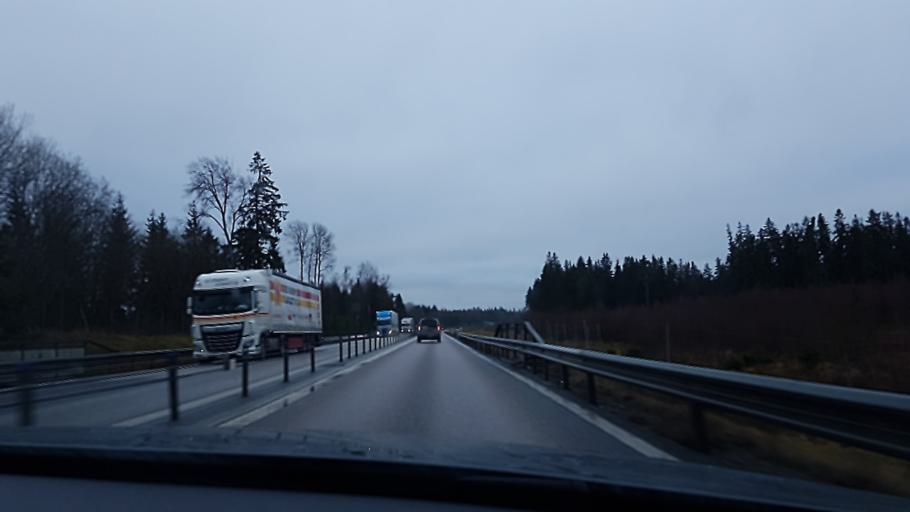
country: SE
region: Kronoberg
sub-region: Ljungby Kommun
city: Lagan
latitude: 56.9781
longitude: 14.0186
